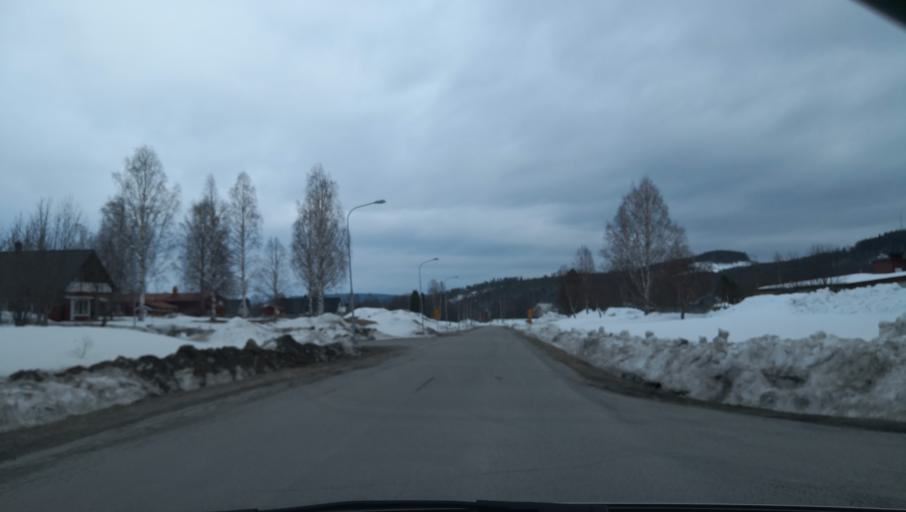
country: SE
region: Vaesterbotten
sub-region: Vannas Kommun
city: Vannasby
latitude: 63.9189
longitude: 19.8087
